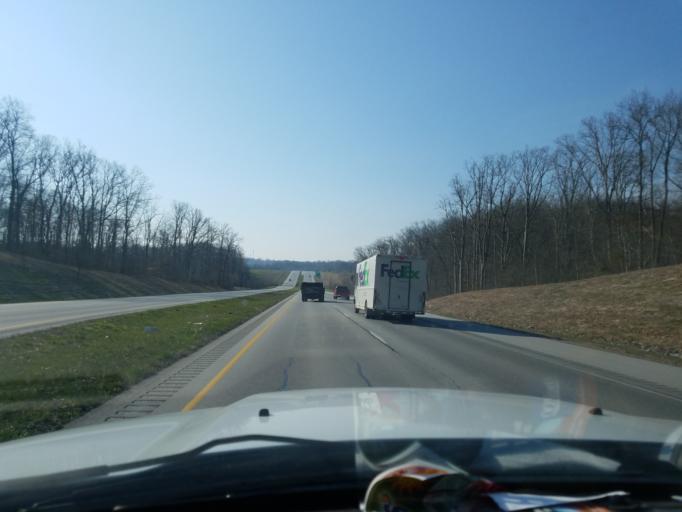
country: US
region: Indiana
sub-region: Monroe County
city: Ellettsville
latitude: 39.2007
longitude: -86.5757
